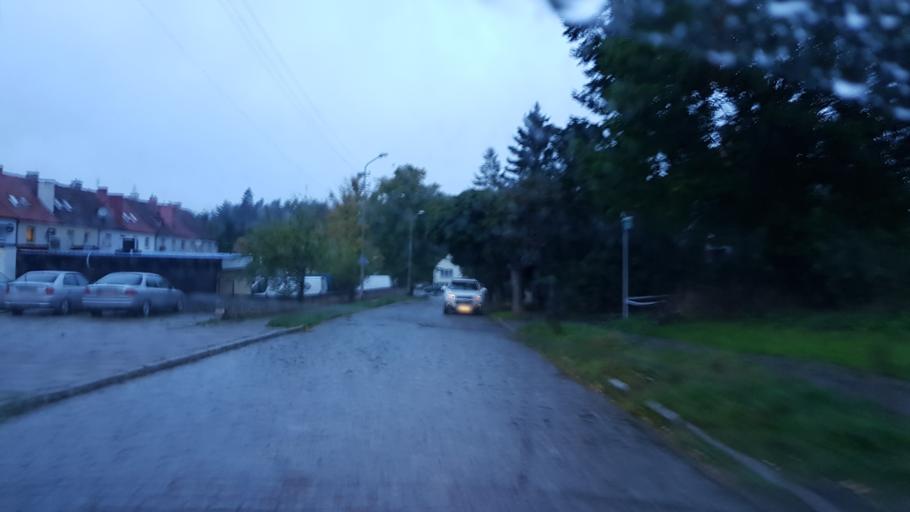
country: PL
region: West Pomeranian Voivodeship
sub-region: Powiat policki
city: Przeclaw
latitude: 53.4122
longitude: 14.5002
